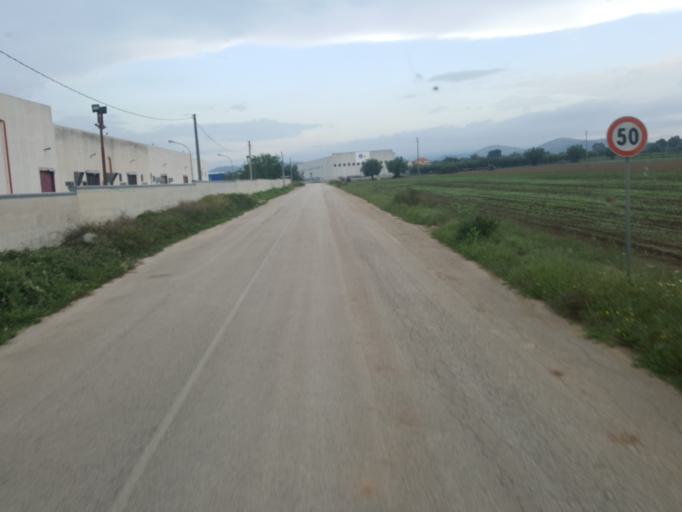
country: IT
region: Campania
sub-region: Provincia di Caserta
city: Pignataro Maggiore
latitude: 41.1737
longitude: 14.1490
